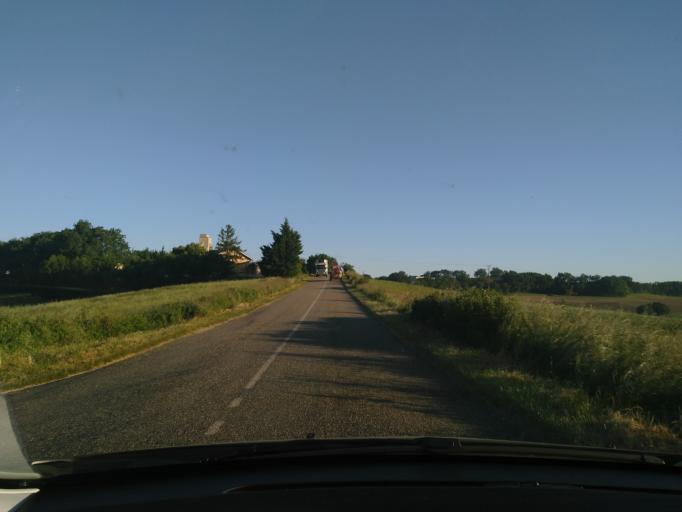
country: FR
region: Midi-Pyrenees
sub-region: Departement du Gers
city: Jegun
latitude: 43.8552
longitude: 0.5235
